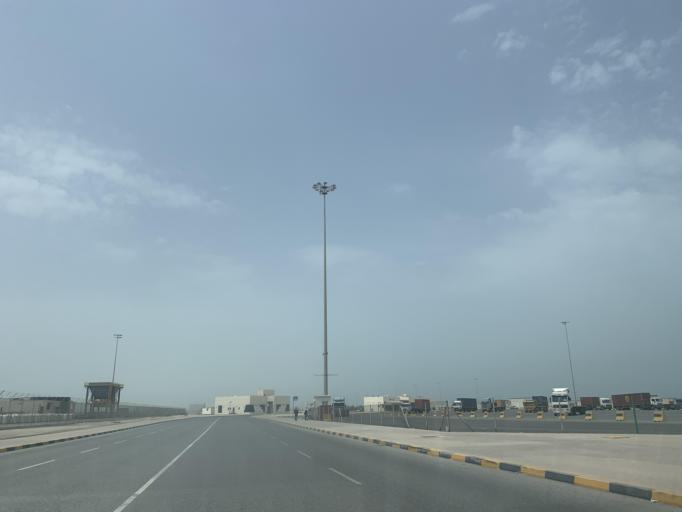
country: BH
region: Muharraq
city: Al Hadd
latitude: 26.1955
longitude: 50.7111
